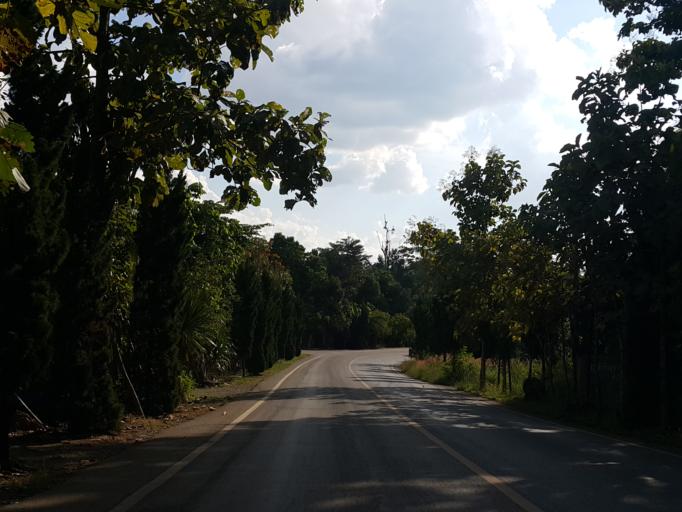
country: TH
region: Chiang Mai
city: Mae On
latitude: 18.8499
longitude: 99.2697
